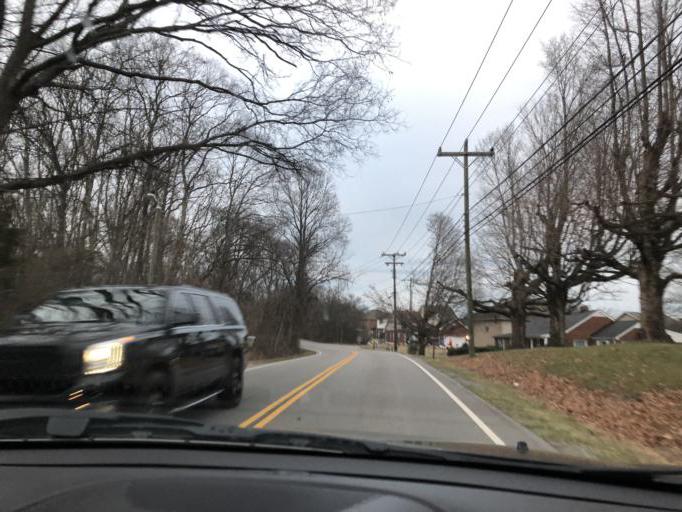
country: US
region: Tennessee
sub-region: Wilson County
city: Green Hill
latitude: 36.1887
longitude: -86.5903
